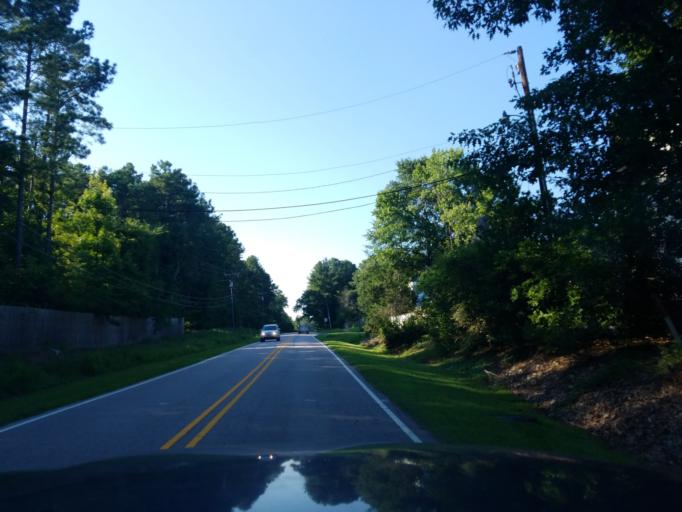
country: US
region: North Carolina
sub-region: Wake County
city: Green Level
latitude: 35.8796
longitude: -78.9151
